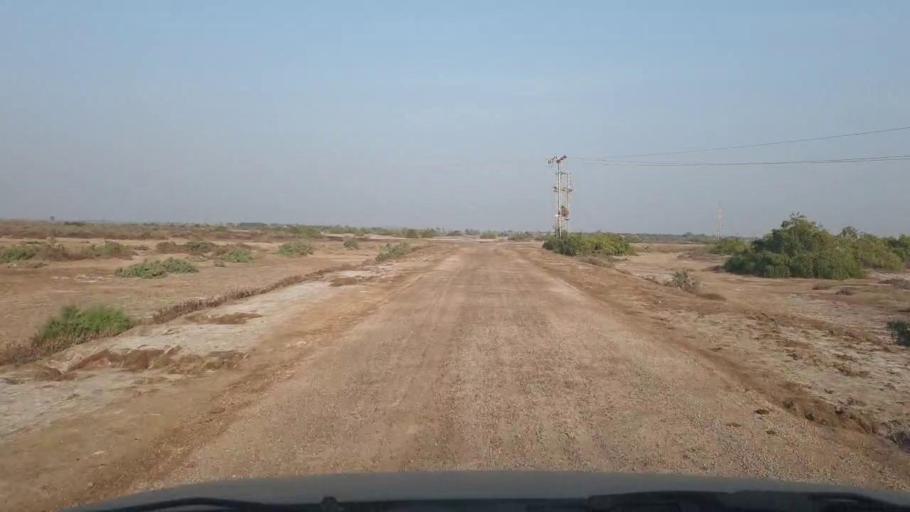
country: PK
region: Sindh
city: Mirwah Gorchani
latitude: 25.2954
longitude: 69.1803
